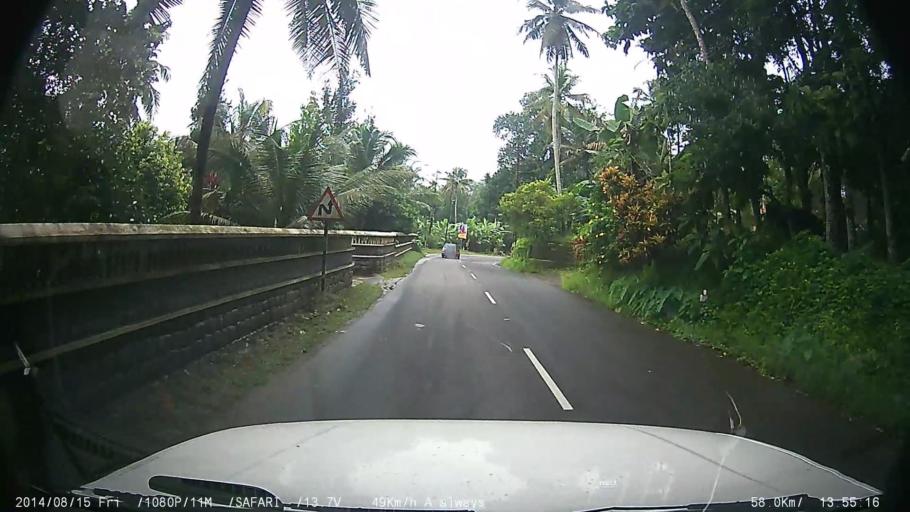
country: IN
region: Kerala
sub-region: Kottayam
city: Palackattumala
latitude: 9.7194
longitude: 76.6550
